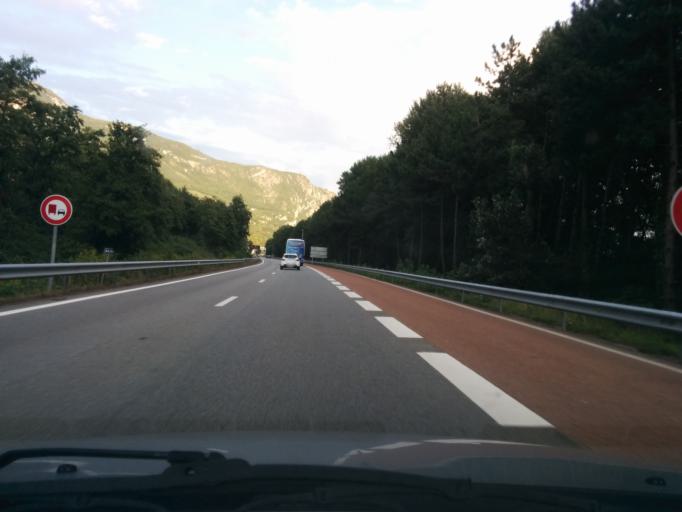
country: FR
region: Rhone-Alpes
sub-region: Departement de l'Isere
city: Fontaine
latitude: 45.2119
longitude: 5.6874
